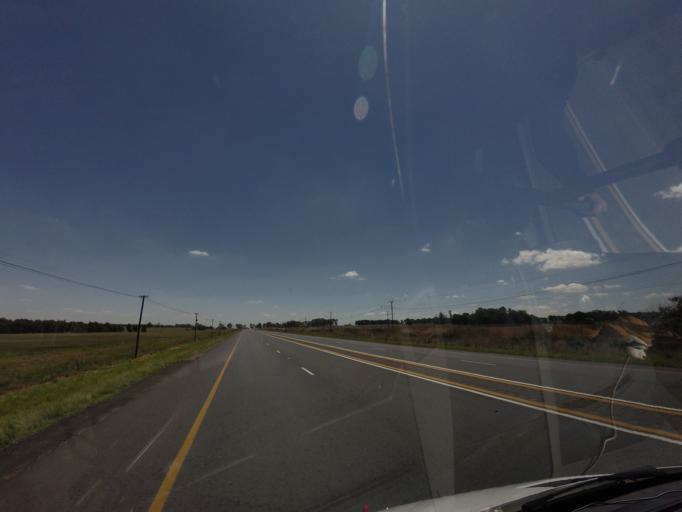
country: ZA
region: Mpumalanga
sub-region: Nkangala District Municipality
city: Belfast
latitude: -25.7334
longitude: 30.0166
